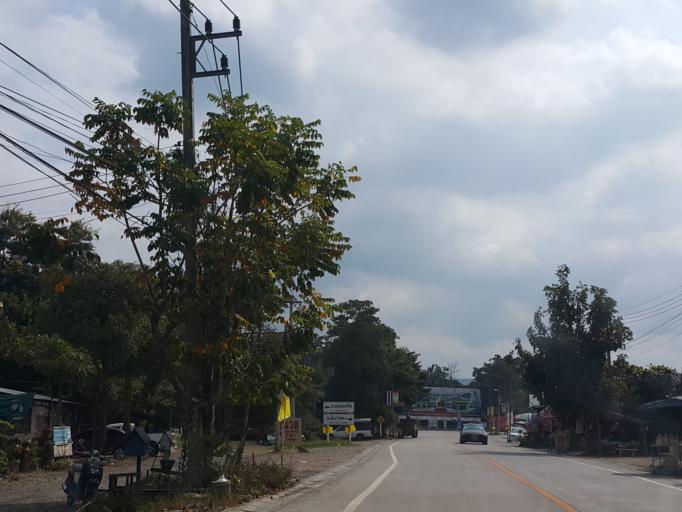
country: TH
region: Chiang Mai
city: Mae On
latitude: 18.7983
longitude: 99.2431
